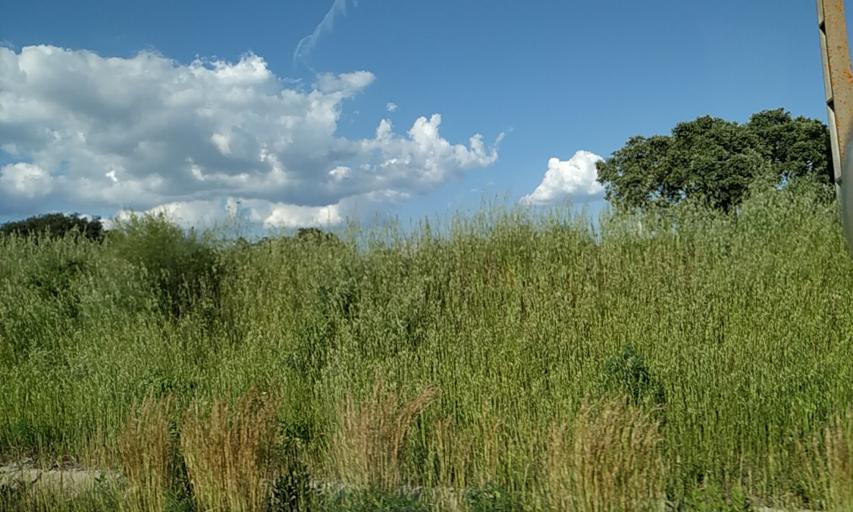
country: PT
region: Portalegre
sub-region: Portalegre
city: Urra
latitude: 39.1422
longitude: -7.4513
